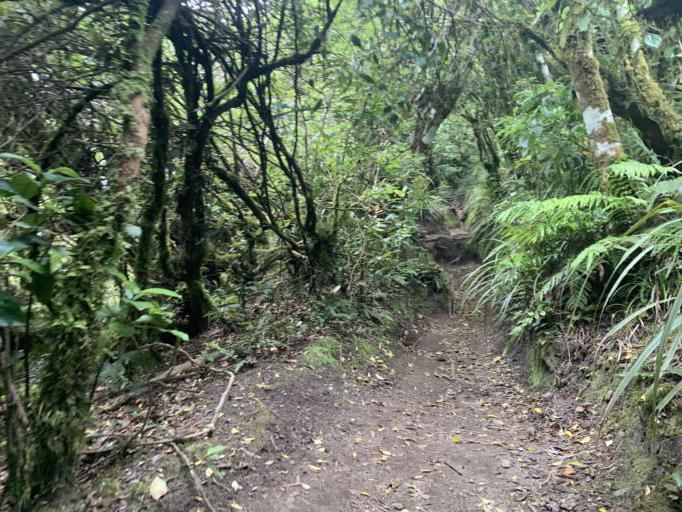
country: NZ
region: Waikato
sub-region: Taupo District
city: Taupo
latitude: -38.6957
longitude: 176.1613
